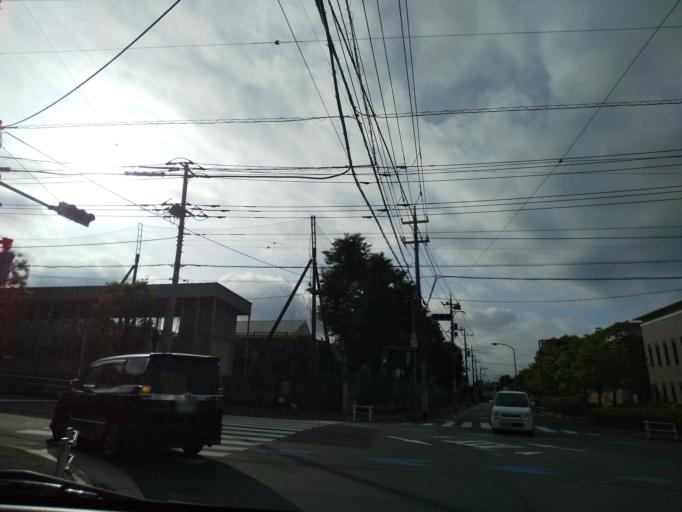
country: JP
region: Tokyo
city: Hachioji
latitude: 35.6823
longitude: 139.3183
